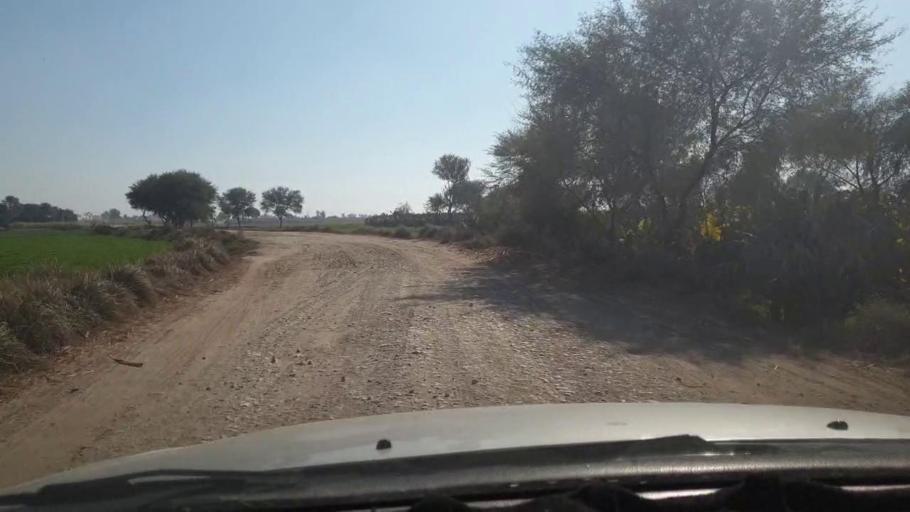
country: PK
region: Sindh
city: Ghotki
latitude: 28.0207
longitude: 69.2225
